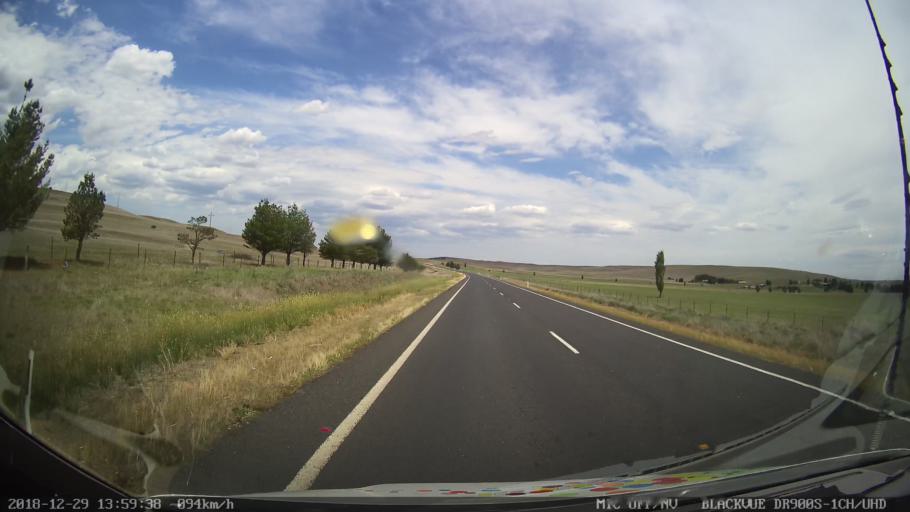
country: AU
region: New South Wales
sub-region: Cooma-Monaro
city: Cooma
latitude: -36.2552
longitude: 149.1502
